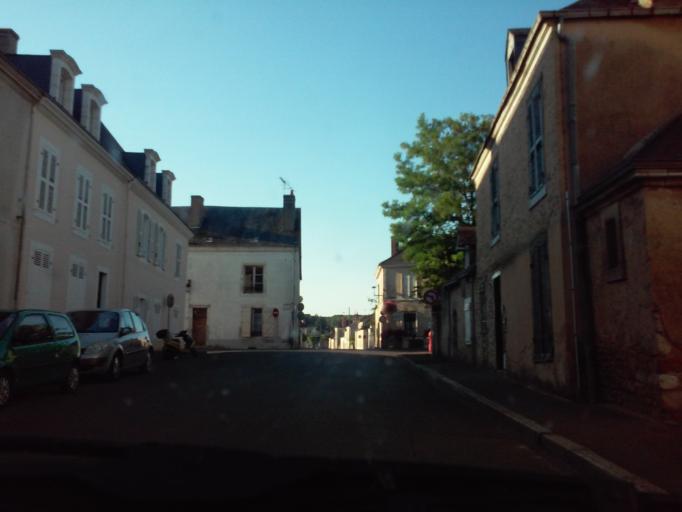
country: FR
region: Pays de la Loire
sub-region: Departement de la Sarthe
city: Montfort-le-Gesnois
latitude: 48.0471
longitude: 0.4169
